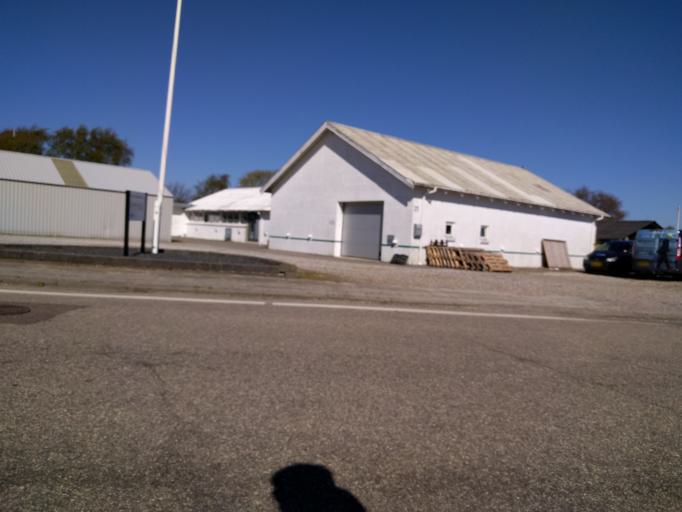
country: DK
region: Central Jutland
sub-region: Ringkobing-Skjern Kommune
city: Ringkobing
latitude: 56.0935
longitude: 8.2528
